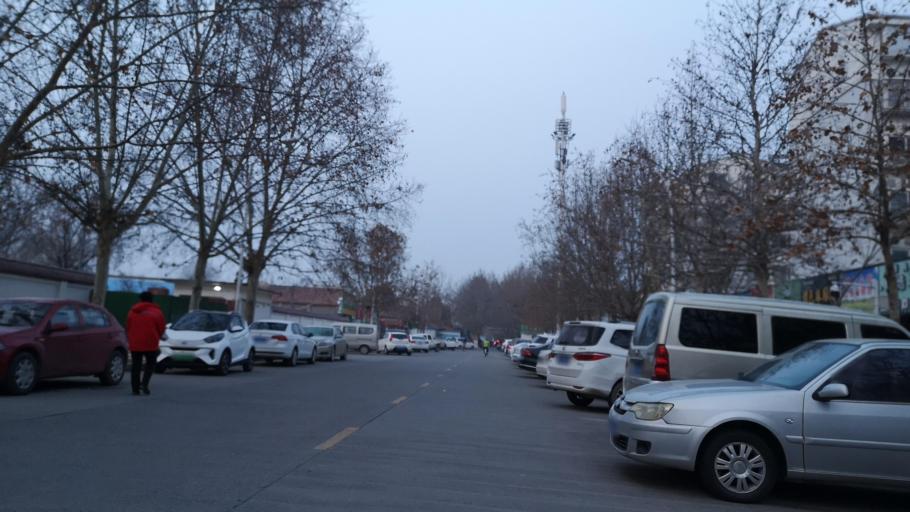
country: CN
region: Henan Sheng
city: Zhongyuanlu
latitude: 35.7562
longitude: 115.0614
